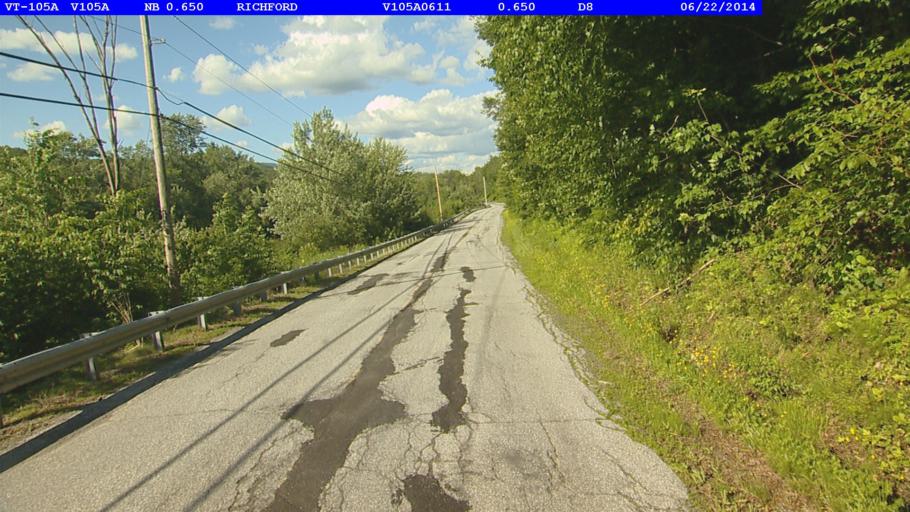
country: US
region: Vermont
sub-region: Franklin County
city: Richford
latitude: 45.0008
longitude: -72.6027
